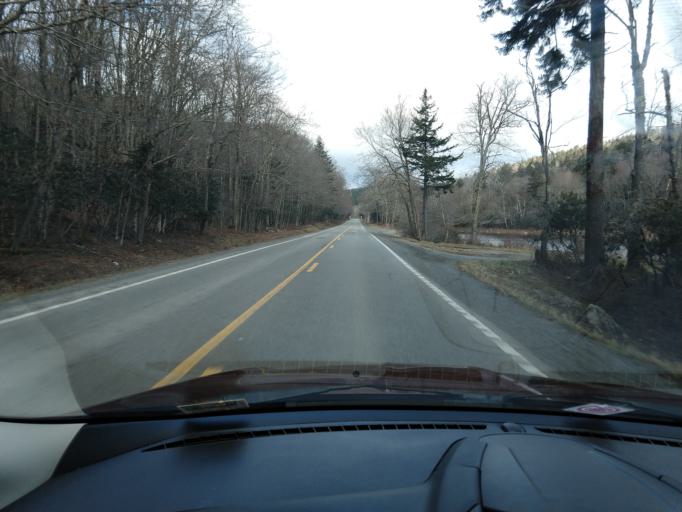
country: US
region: West Virginia
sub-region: Randolph County
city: Elkins
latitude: 38.6300
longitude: -79.8746
